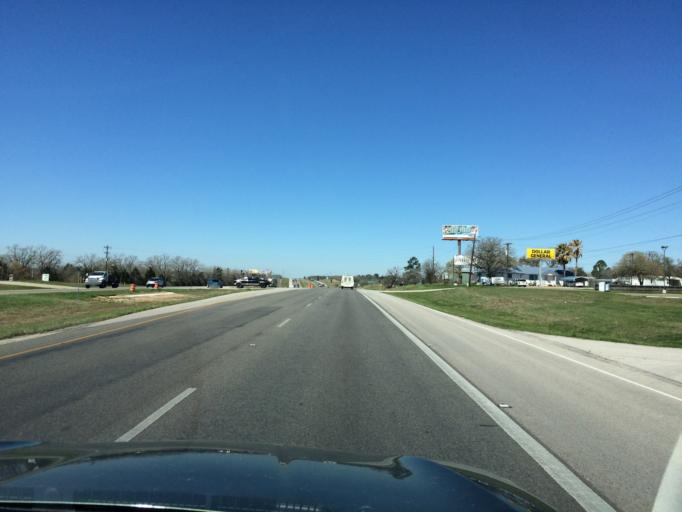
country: US
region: Texas
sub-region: Bastrop County
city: Wyldwood
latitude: 30.1279
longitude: -97.4423
